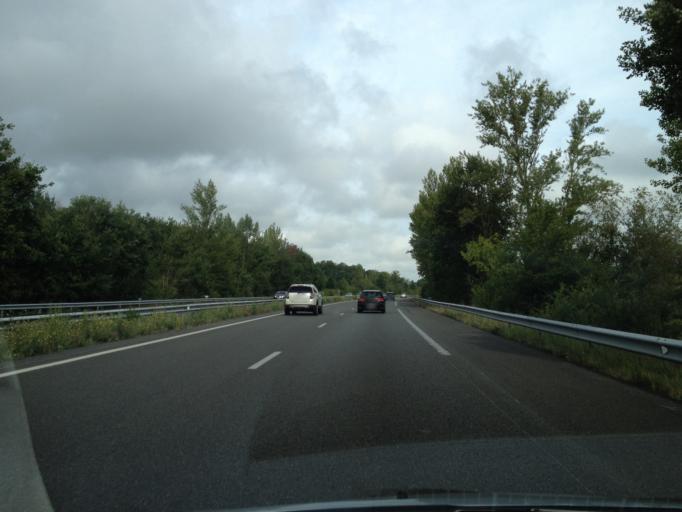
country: FR
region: Aquitaine
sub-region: Departement du Lot-et-Garonne
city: Layrac
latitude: 44.1111
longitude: 0.7330
